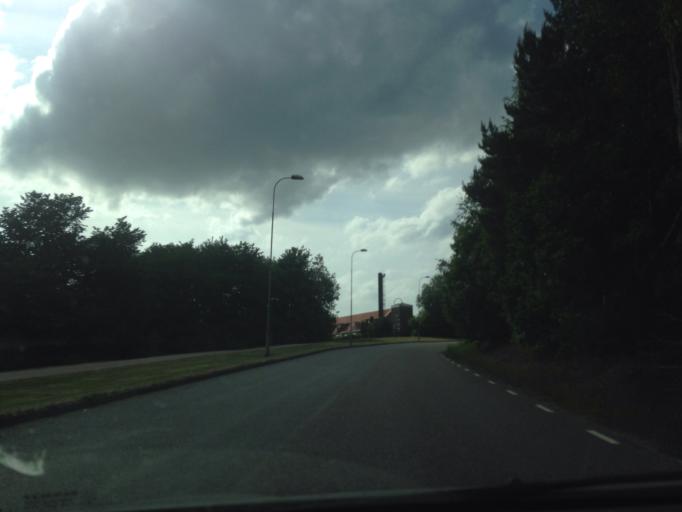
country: SE
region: Vaestra Goetaland
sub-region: Goteborg
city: Goeteborg
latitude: 57.7628
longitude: 11.9320
